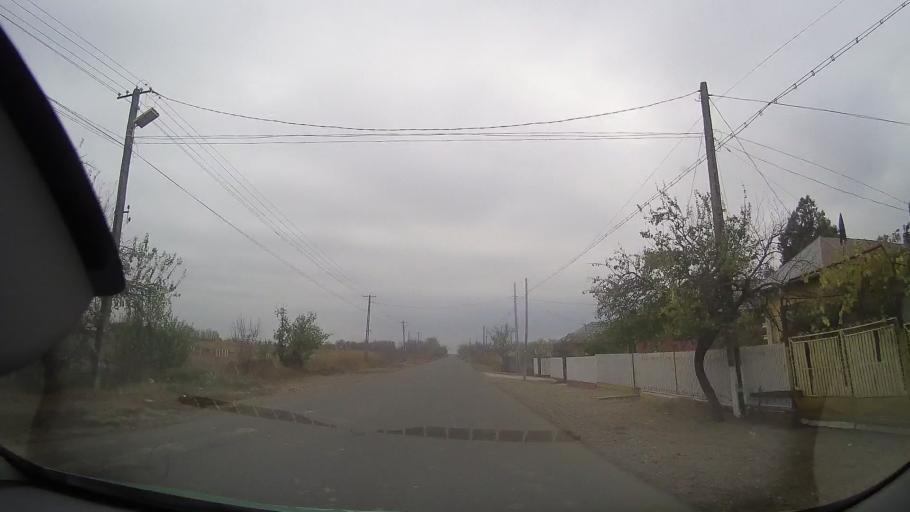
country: RO
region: Buzau
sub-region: Comuna Pogoanele
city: Pogoanele
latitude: 44.9063
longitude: 26.9802
